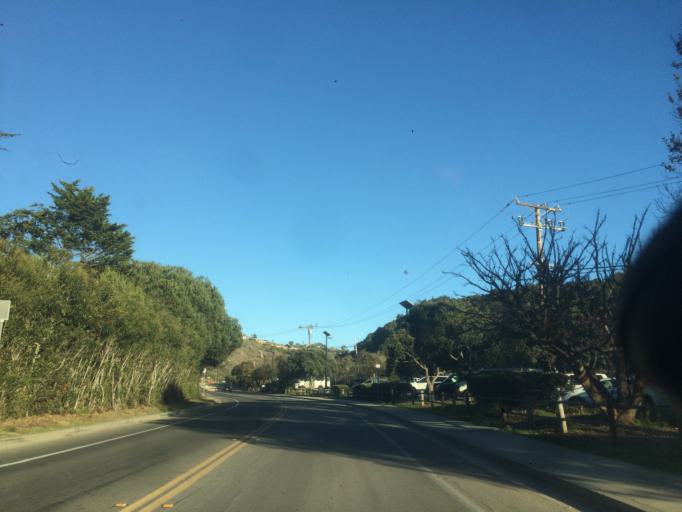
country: US
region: California
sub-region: Santa Barbara County
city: Santa Barbara
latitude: 34.4044
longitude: -119.7428
